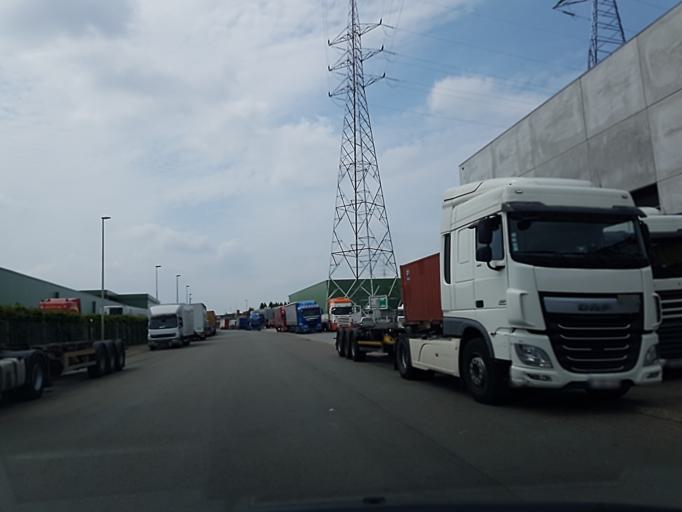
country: BE
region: Flanders
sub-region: Provincie Antwerpen
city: Schoten
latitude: 51.2365
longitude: 4.4610
